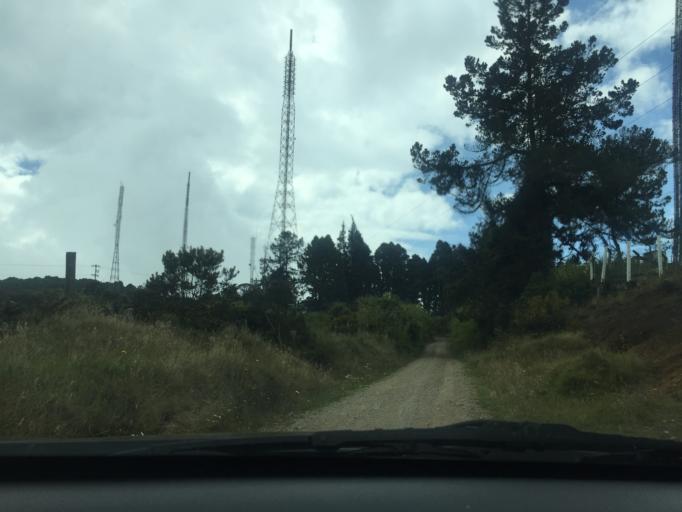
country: CO
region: Cundinamarca
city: Facatativa
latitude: 4.8016
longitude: -74.3884
